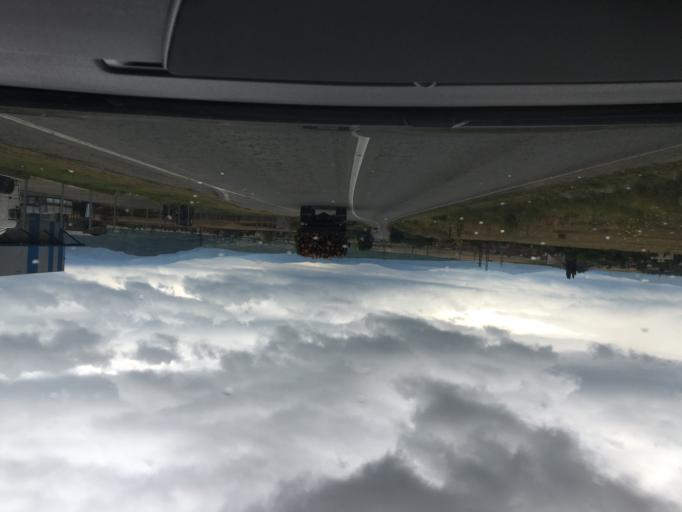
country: BG
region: Kyustendil
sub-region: Obshtina Kyustendil
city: Kyustendil
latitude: 42.2899
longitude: 22.7214
